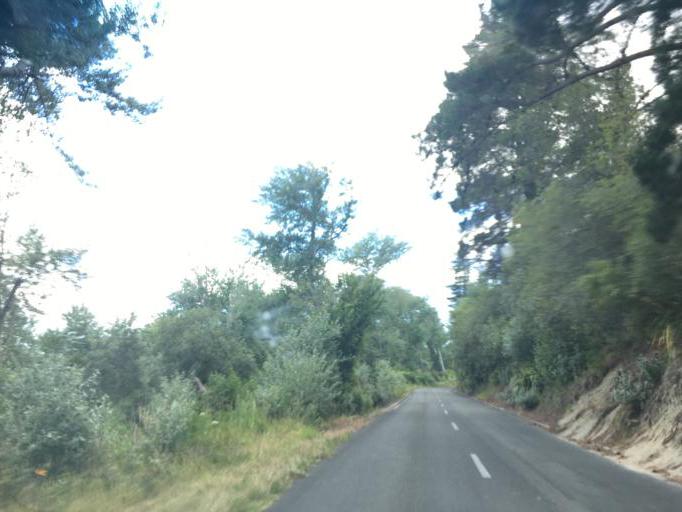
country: NZ
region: Hawke's Bay
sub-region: Hastings District
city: Hastings
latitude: -39.7344
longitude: 176.9038
